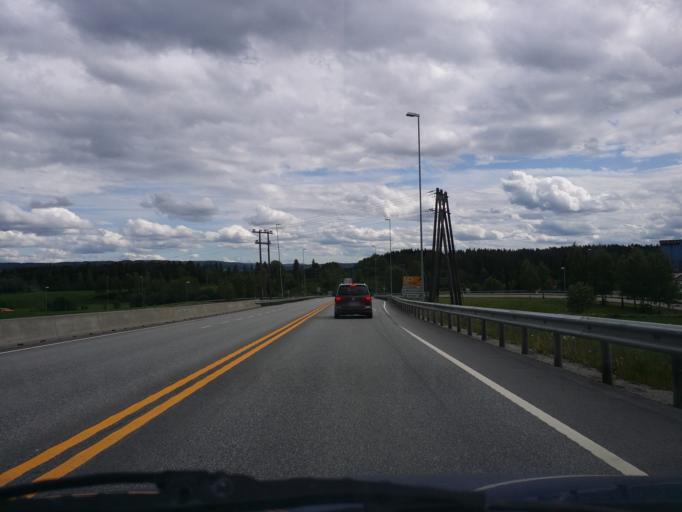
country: NO
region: Hedmark
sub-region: Stange
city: Stange
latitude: 60.7242
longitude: 11.2292
